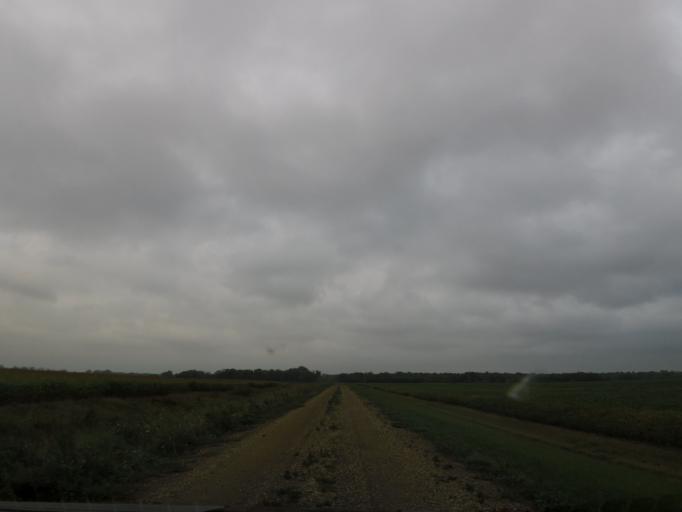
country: US
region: North Dakota
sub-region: Walsh County
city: Grafton
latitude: 48.5284
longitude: -97.1666
